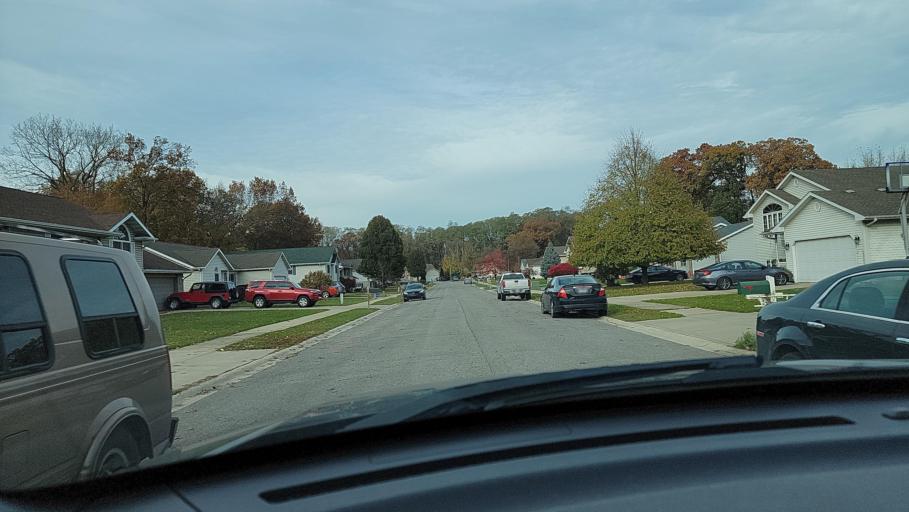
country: US
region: Indiana
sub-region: Porter County
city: Portage
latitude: 41.5955
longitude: -87.1592
